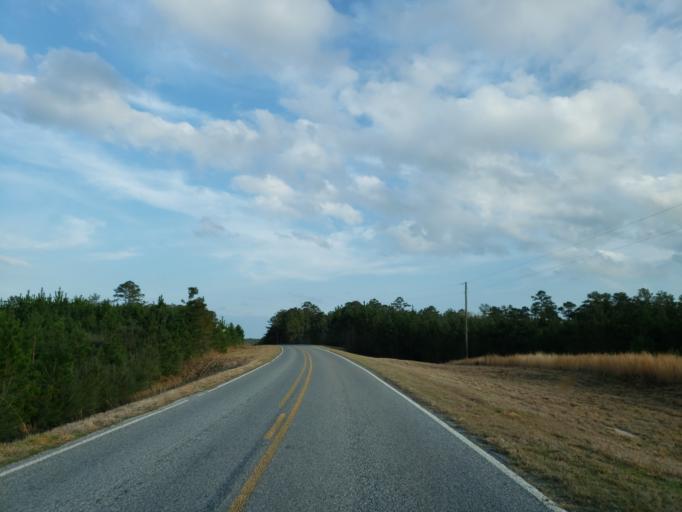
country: US
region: Mississippi
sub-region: Clarke County
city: Stonewall
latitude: 32.1757
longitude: -88.7026
